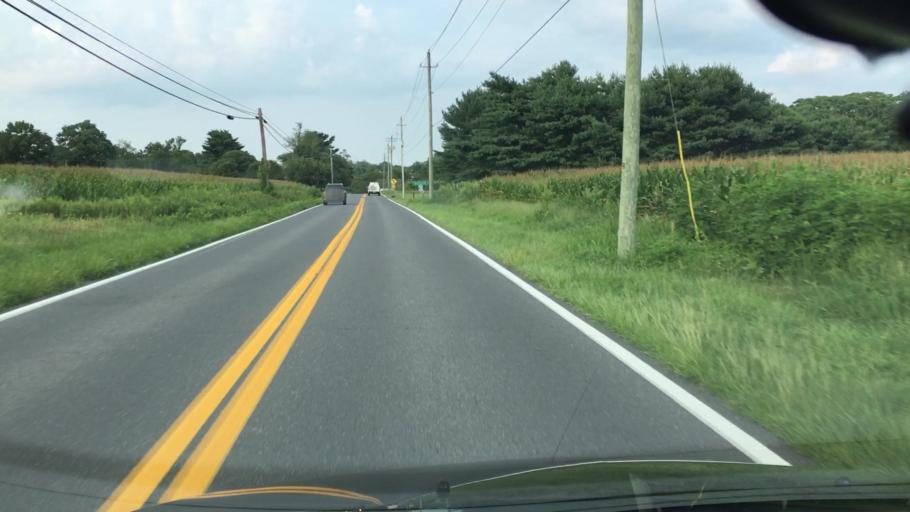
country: US
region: Delaware
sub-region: Sussex County
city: Selbyville
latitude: 38.4397
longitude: -75.1972
